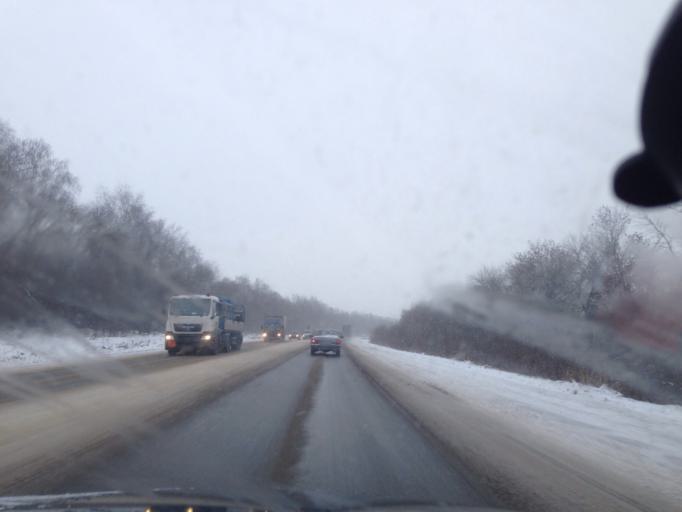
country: RU
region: Tula
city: Bolokhovo
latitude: 54.1045
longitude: 37.7603
